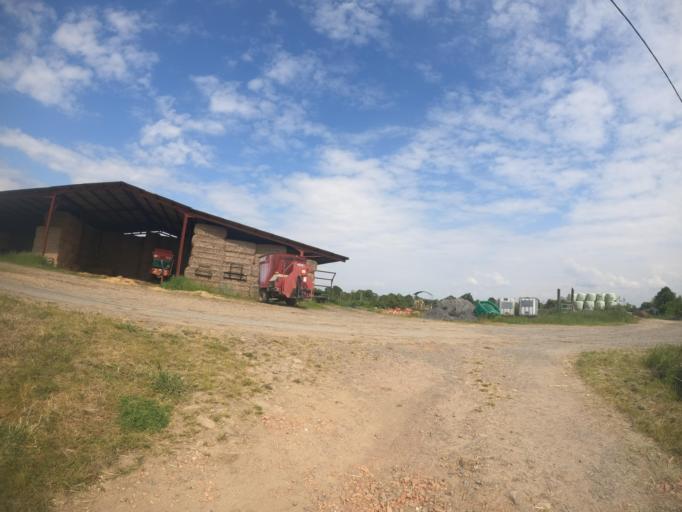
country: FR
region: Poitou-Charentes
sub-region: Departement des Deux-Sevres
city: Saint-Varent
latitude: 46.8891
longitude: -0.2757
